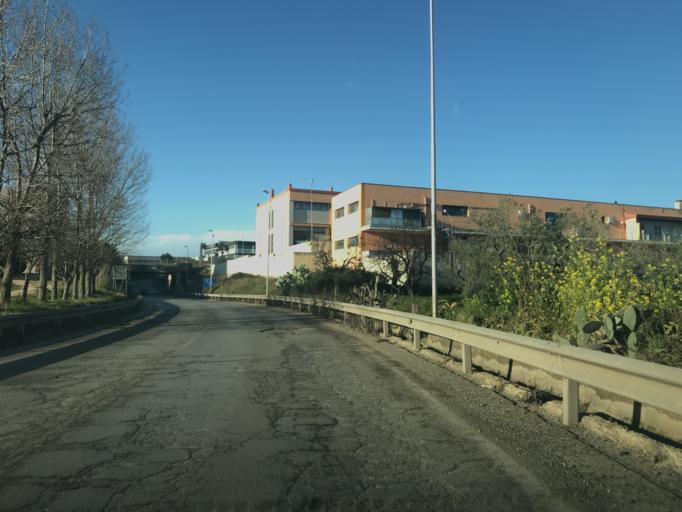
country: IT
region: Apulia
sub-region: Provincia di Bari
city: Corato
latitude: 41.1371
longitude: 16.4166
